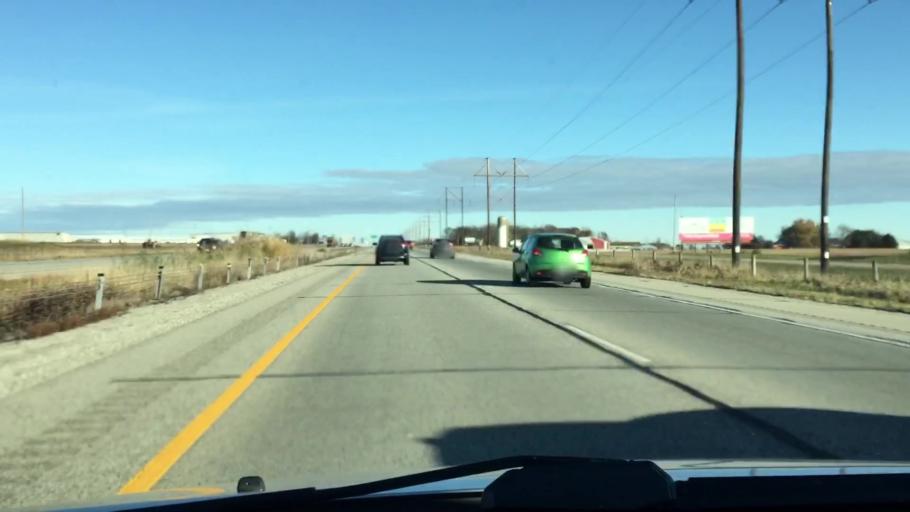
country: US
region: Wisconsin
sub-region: Winnebago County
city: Oshkosh
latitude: 43.9335
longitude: -88.5832
